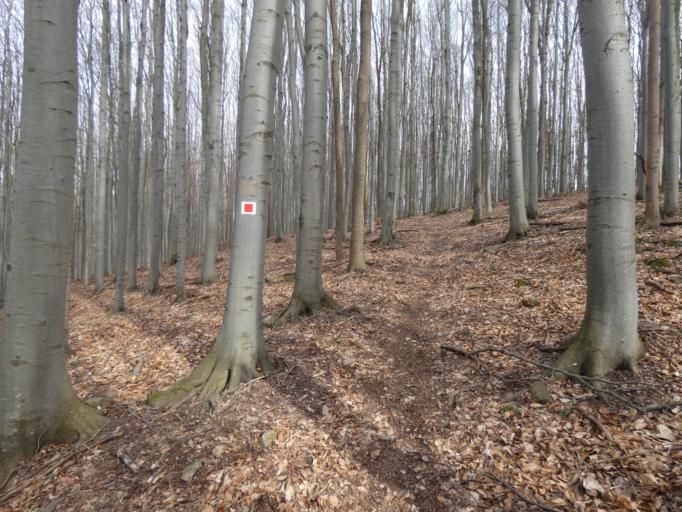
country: HU
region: Nograd
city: Diosjeno
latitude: 47.9588
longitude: 18.9469
